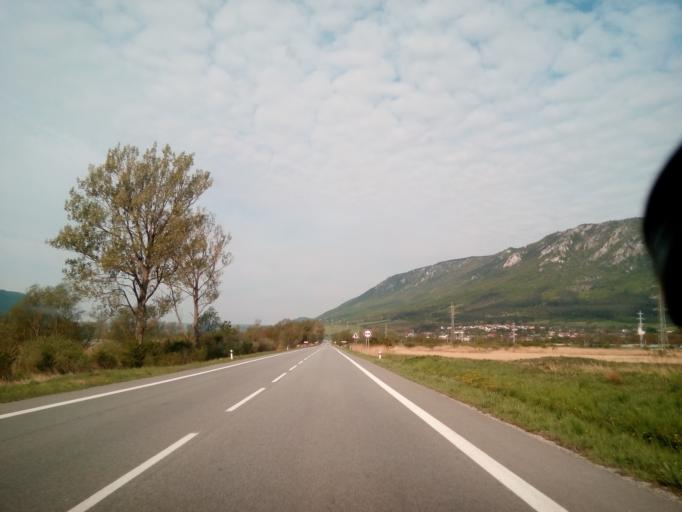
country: SK
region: Kosicky
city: Medzev
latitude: 48.6009
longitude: 20.7634
